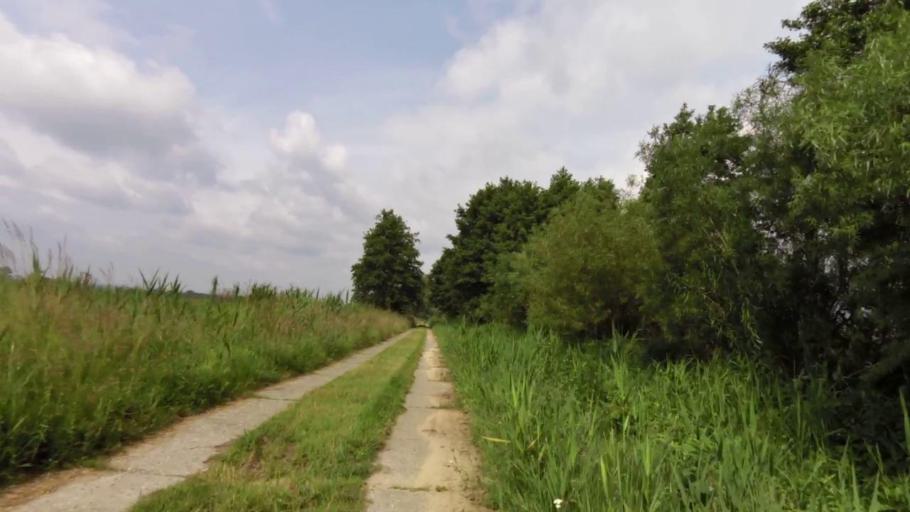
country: PL
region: West Pomeranian Voivodeship
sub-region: Powiat goleniowski
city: Stepnica
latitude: 53.5524
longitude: 14.6933
